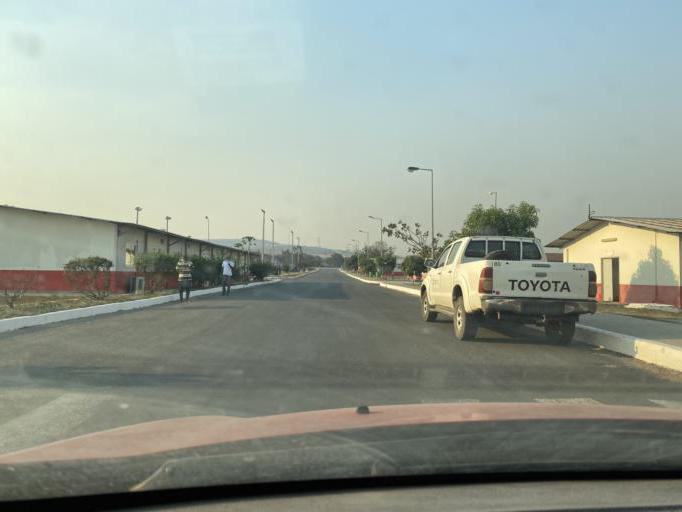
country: AO
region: Cuanza Norte
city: N'dalatando
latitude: -9.7427
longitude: 15.1408
